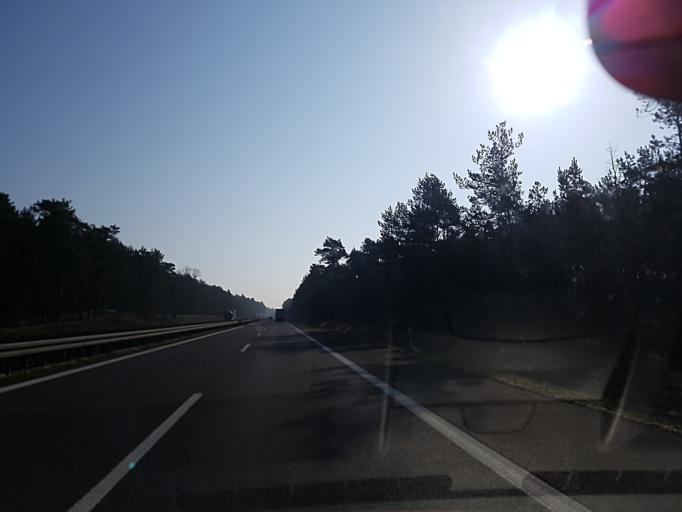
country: DE
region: Brandenburg
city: Forst
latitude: 51.7117
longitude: 14.5820
